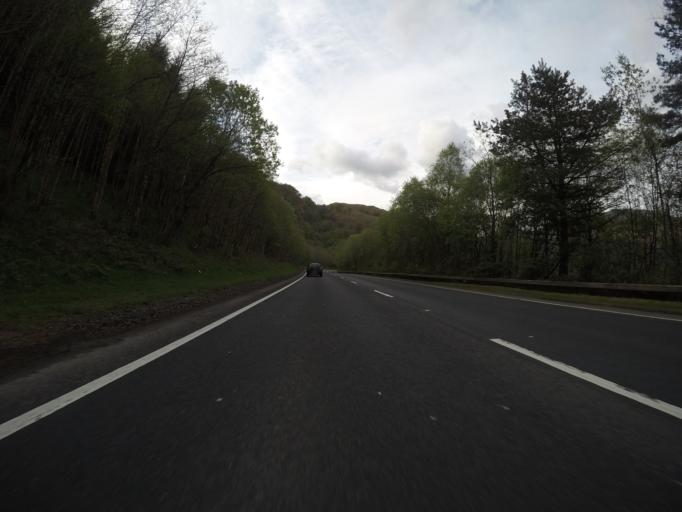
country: GB
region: Scotland
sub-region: Argyll and Bute
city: Helensburgh
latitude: 56.1557
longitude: -4.6702
